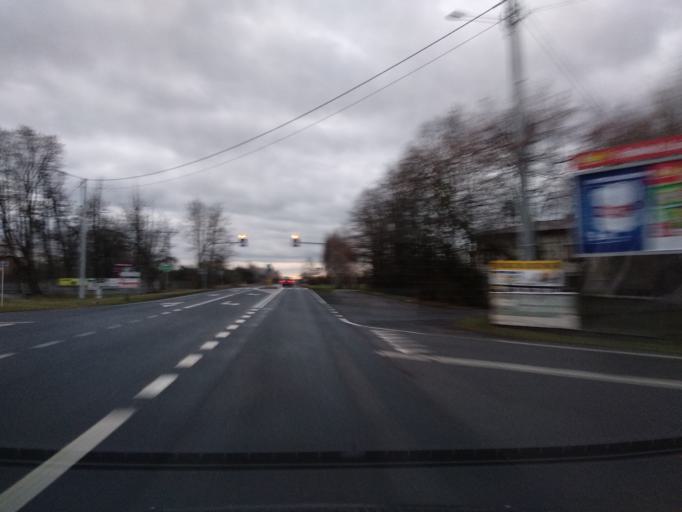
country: PL
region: Greater Poland Voivodeship
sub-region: Powiat koninski
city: Rychwal
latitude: 52.0782
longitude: 18.1601
